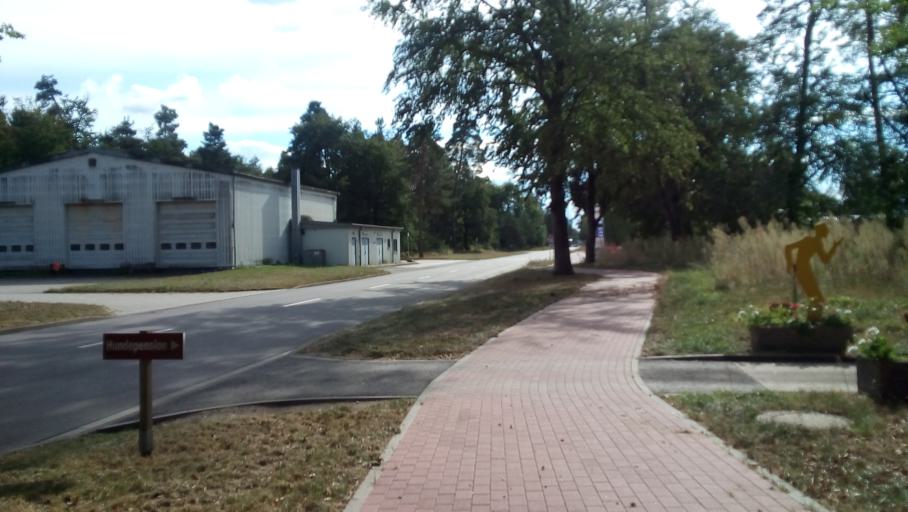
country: DE
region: Baden-Wuerttemberg
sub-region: Karlsruhe Region
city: Hugelsheim
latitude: 48.7781
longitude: 8.0939
